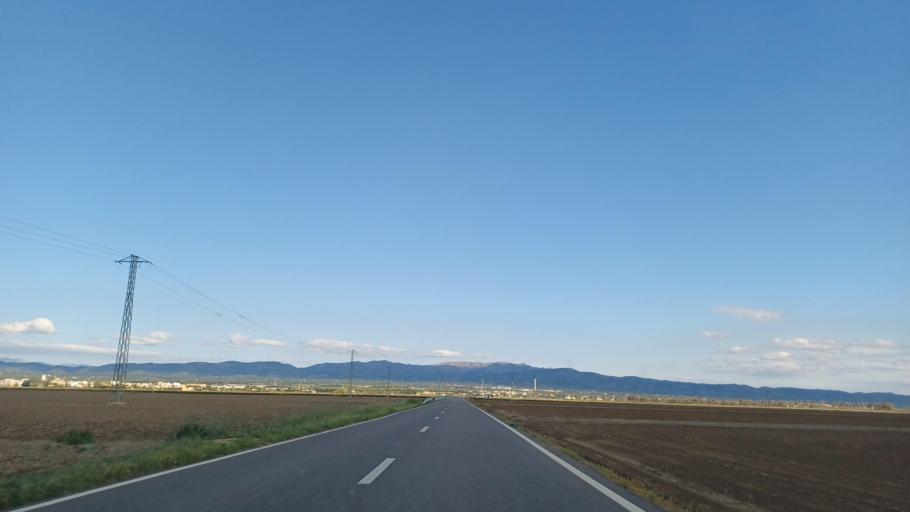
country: ES
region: Catalonia
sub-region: Provincia de Tarragona
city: Deltebre
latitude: 40.7623
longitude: 0.6966
